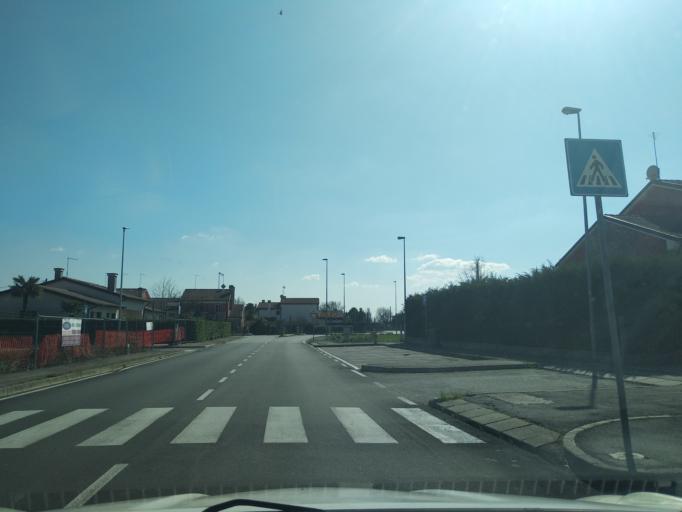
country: IT
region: Veneto
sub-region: Provincia di Padova
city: Villafranca Padovana
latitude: 45.4918
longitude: 11.7887
